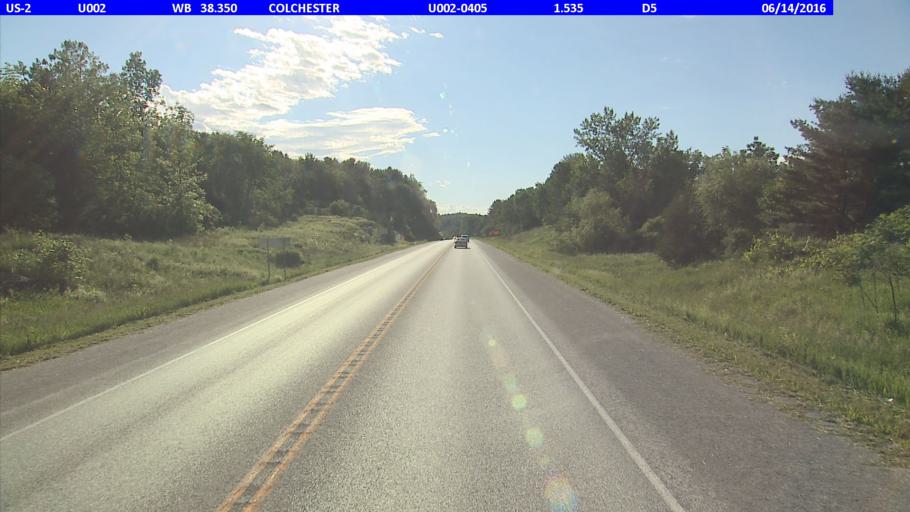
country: US
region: Vermont
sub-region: Chittenden County
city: Colchester
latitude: 44.5923
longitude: -73.1794
